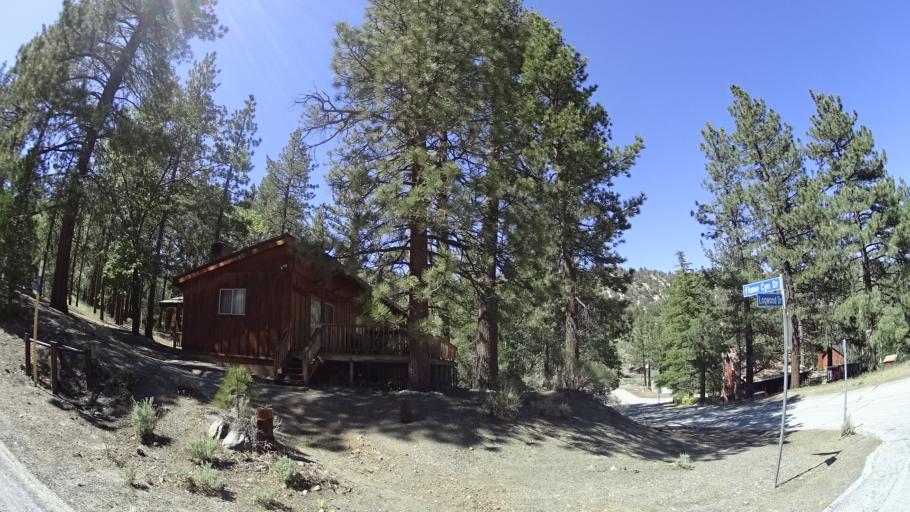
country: US
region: California
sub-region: San Bernardino County
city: Wrightwood
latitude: 34.3647
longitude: -117.6540
